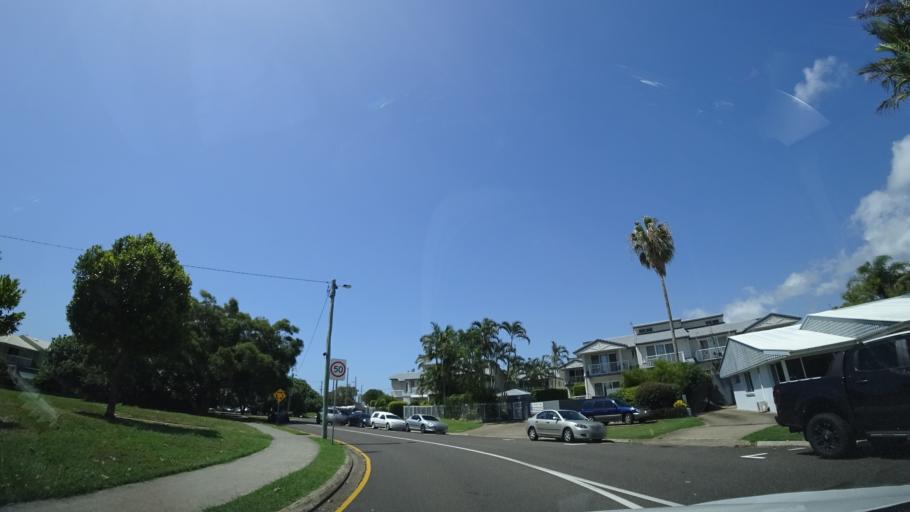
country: AU
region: Queensland
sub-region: Sunshine Coast
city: Mooloolaba
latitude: -26.6553
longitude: 153.0989
